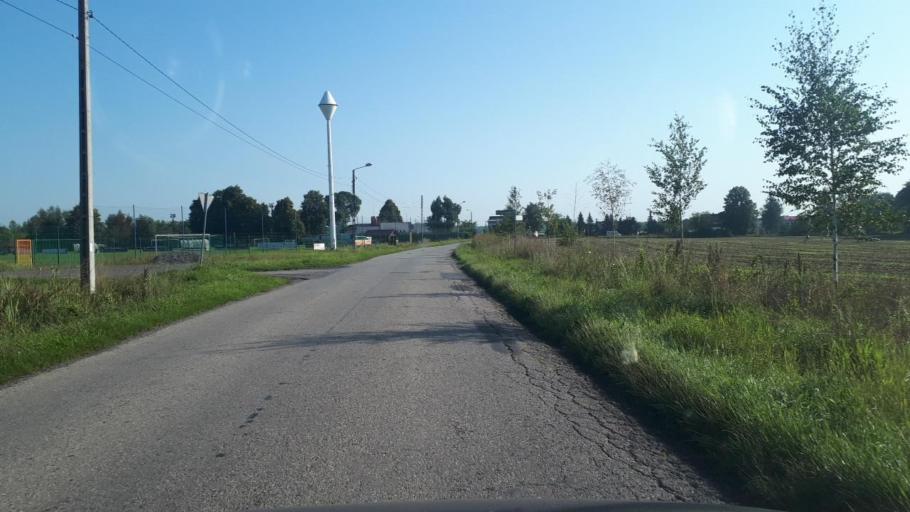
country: PL
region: Silesian Voivodeship
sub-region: Powiat cieszynski
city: Chybie
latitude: 49.8782
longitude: 18.8700
